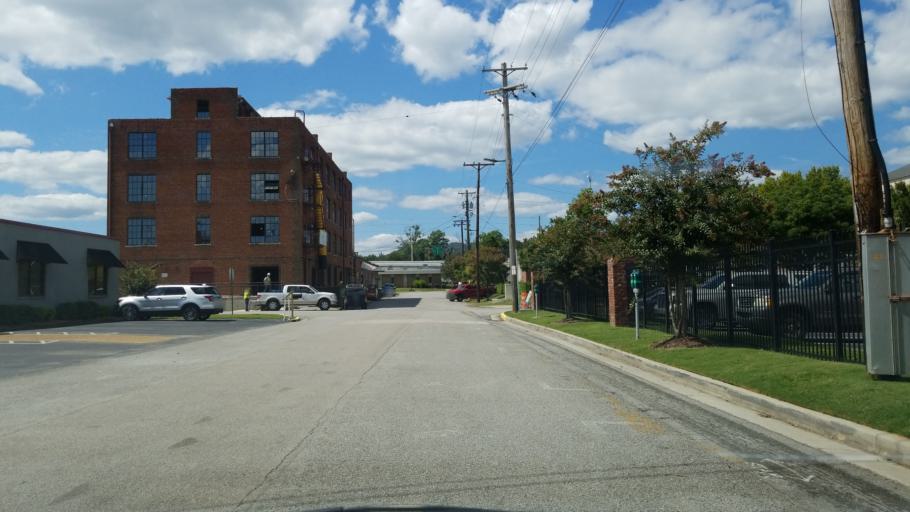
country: US
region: Tennessee
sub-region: Hamilton County
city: Chattanooga
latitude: 35.0397
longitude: -85.3133
